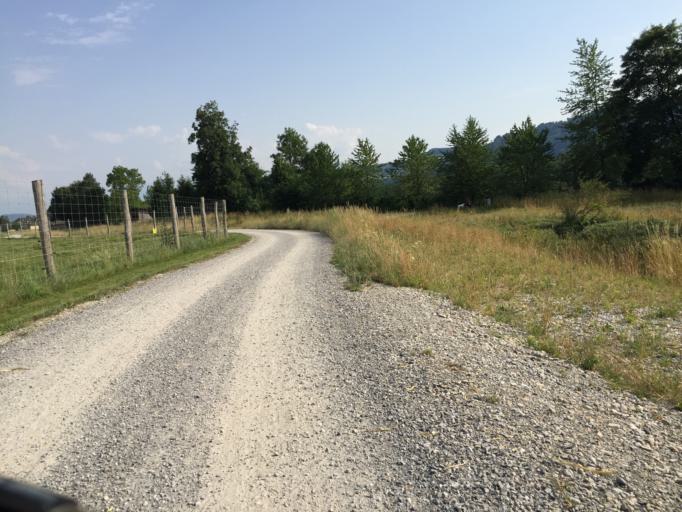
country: CH
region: Bern
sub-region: Bern-Mittelland District
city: Rubigen
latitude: 46.8894
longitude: 7.5468
